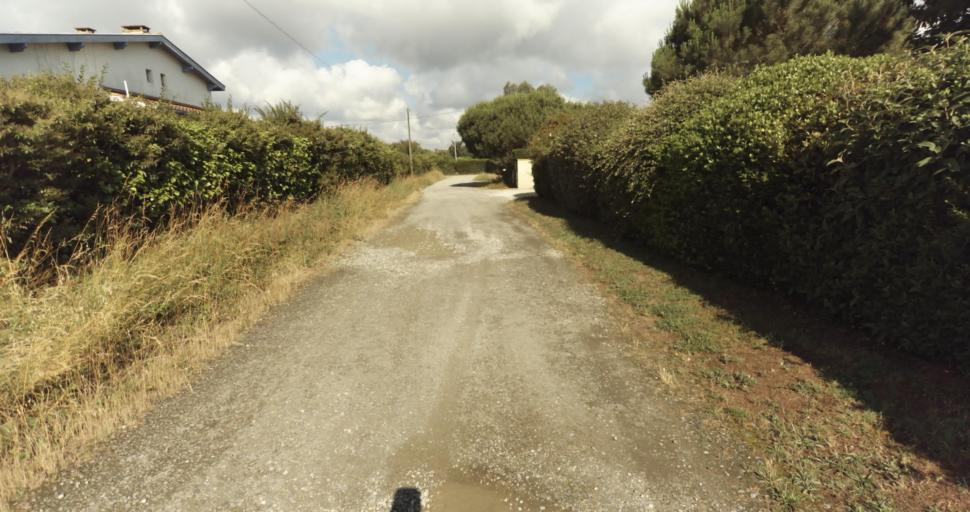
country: FR
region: Midi-Pyrenees
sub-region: Departement de la Haute-Garonne
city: Fontenilles
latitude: 43.5629
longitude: 1.2104
